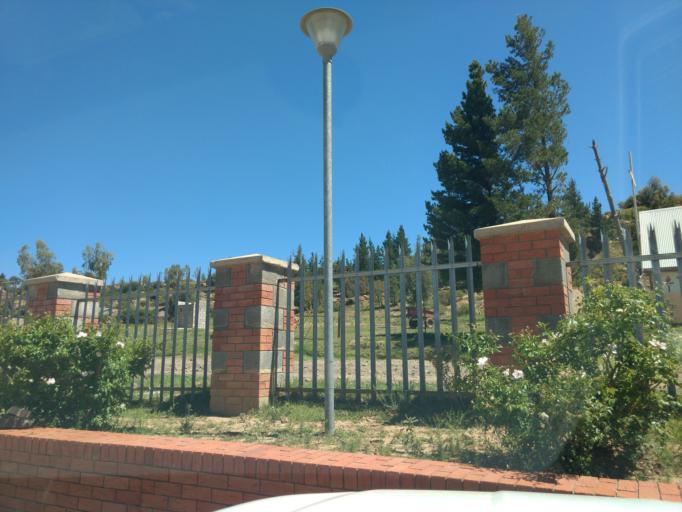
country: LS
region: Maseru
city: Maseru
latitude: -29.4958
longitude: 27.3755
